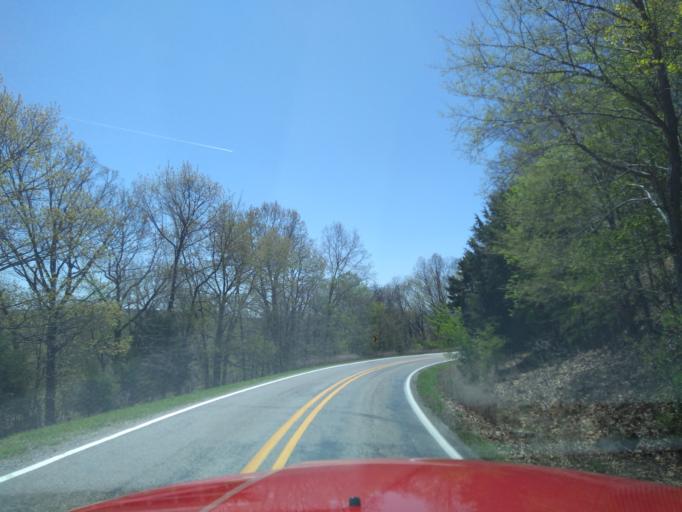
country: US
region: Arkansas
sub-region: Washington County
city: West Fork
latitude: 35.7878
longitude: -94.2547
